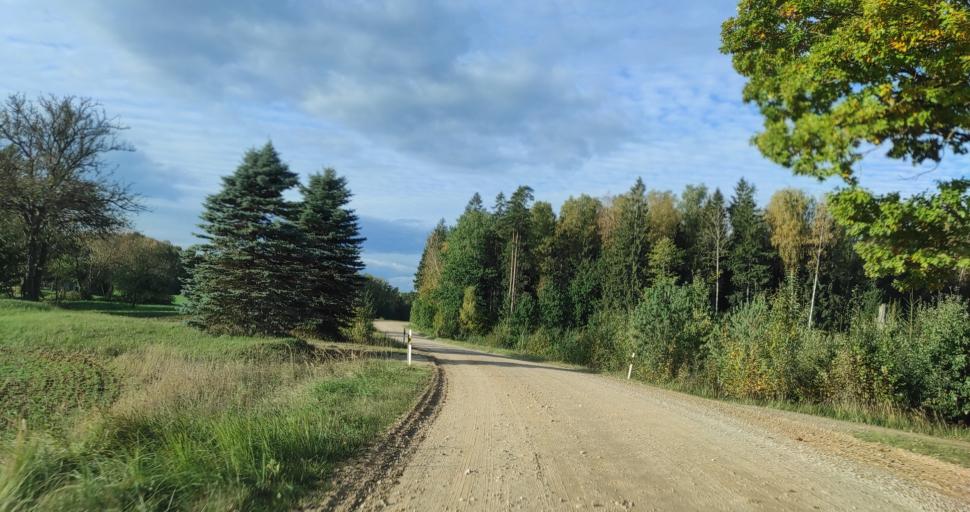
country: LV
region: Skrunda
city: Skrunda
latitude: 56.7477
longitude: 21.8288
